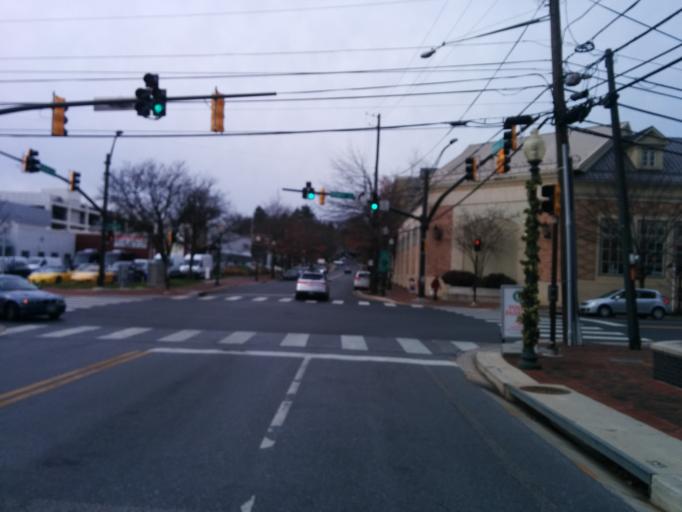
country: US
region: Maryland
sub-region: Montgomery County
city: Bethesda
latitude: 38.9809
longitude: -77.0981
